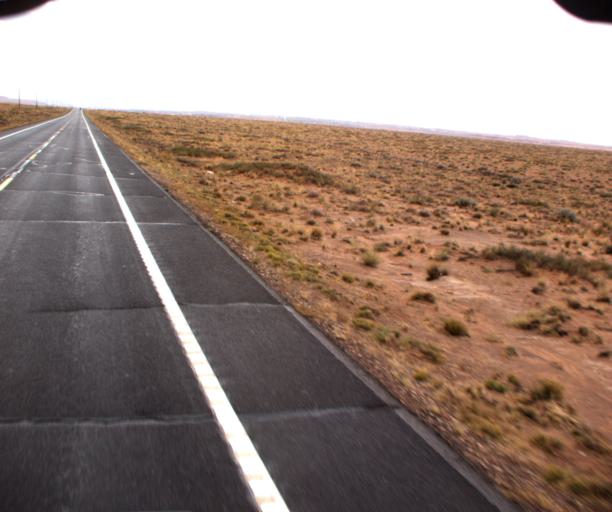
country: US
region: Arizona
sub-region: Coconino County
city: Tuba City
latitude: 36.1428
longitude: -111.1554
